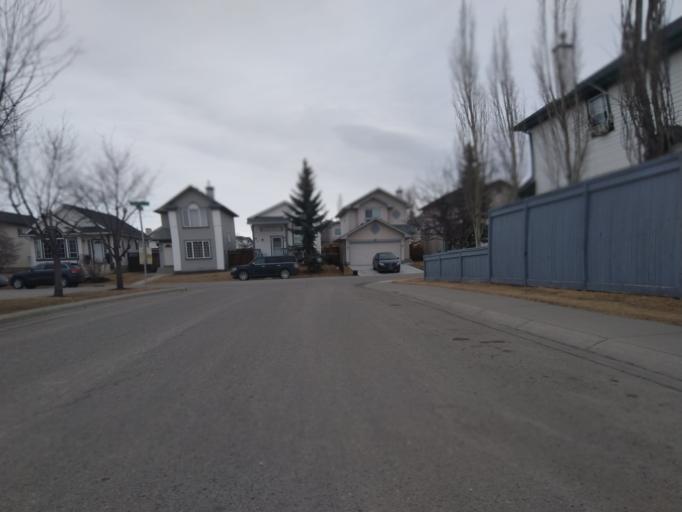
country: CA
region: Alberta
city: Calgary
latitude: 51.1656
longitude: -114.0455
